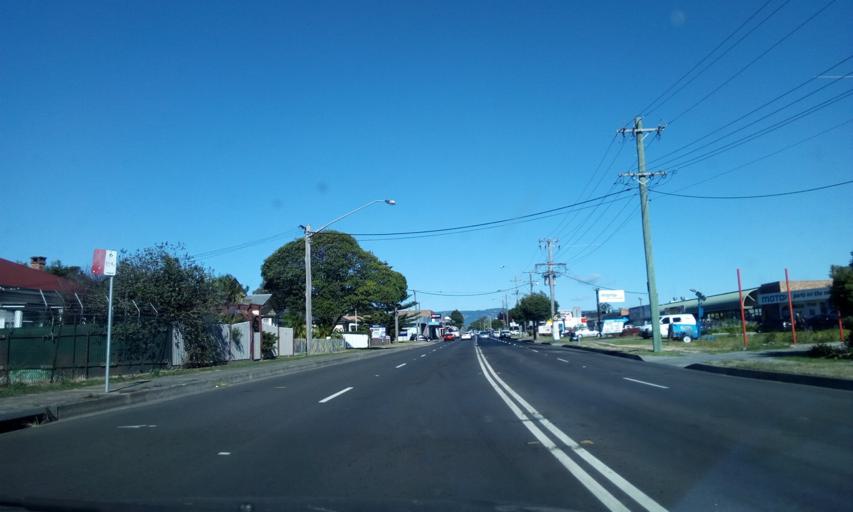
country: AU
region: New South Wales
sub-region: Wollongong
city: Koonawarra
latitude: -34.4908
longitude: 150.7968
